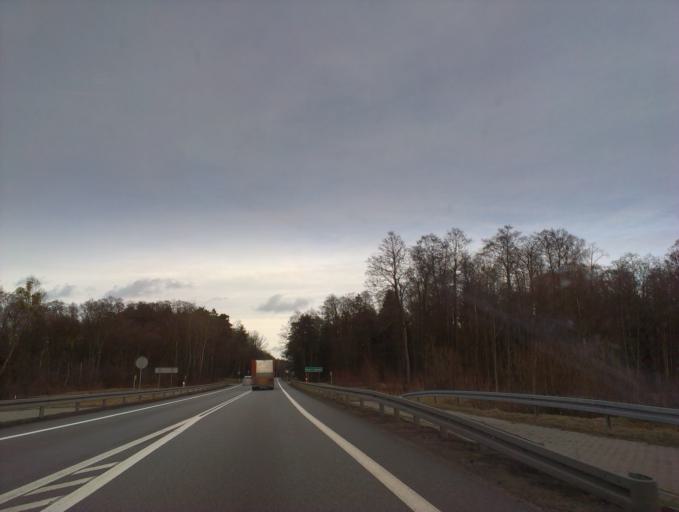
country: PL
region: Kujawsko-Pomorskie
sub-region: Powiat lipnowski
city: Skepe
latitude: 52.8825
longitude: 19.3858
